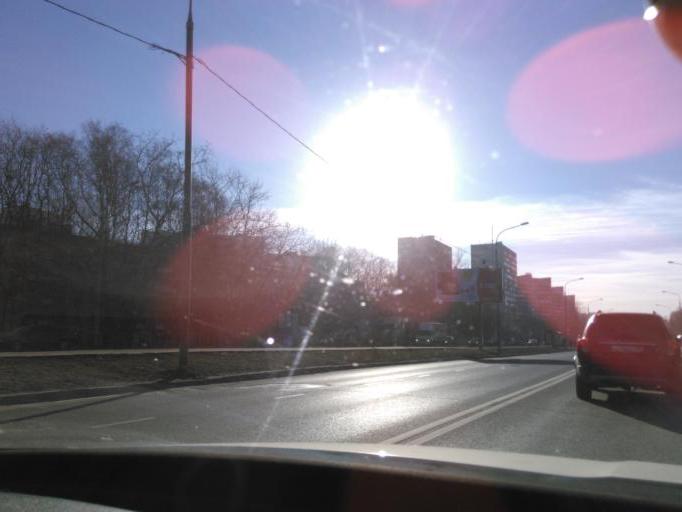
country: RU
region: Moscow
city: Novokhovrino
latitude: 55.8603
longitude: 37.5078
